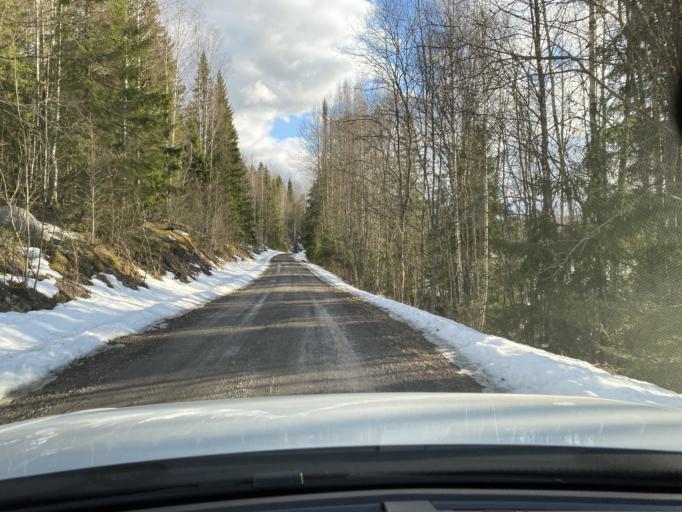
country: FI
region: Pirkanmaa
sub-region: Lounais-Pirkanmaa
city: Mouhijaervi
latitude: 61.4506
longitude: 22.9592
